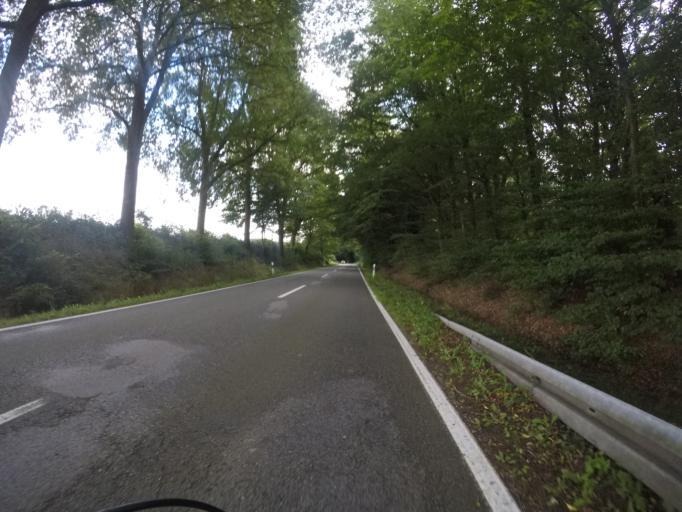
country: DE
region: North Rhine-Westphalia
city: Enger
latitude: 52.0920
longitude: 8.6036
